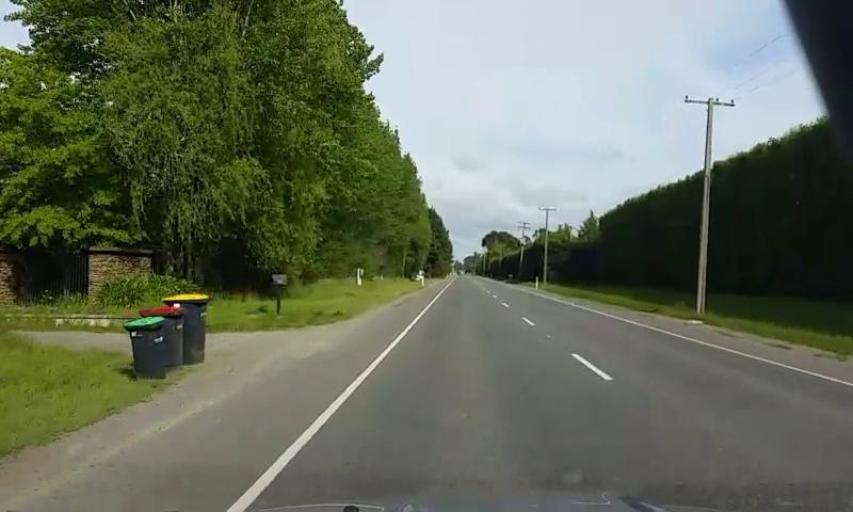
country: NZ
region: Canterbury
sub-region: Selwyn District
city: Prebbleton
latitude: -43.5156
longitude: 172.5186
